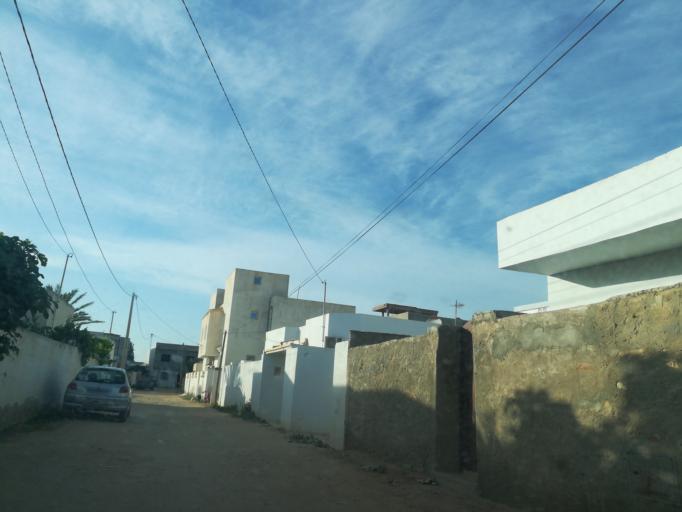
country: TN
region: Safaqis
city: Al Qarmadah
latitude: 34.8131
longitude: 10.7493
